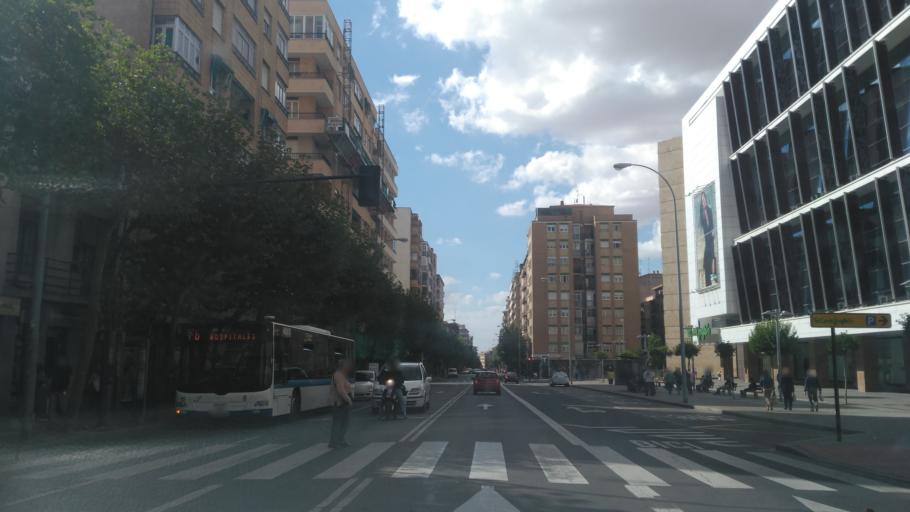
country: ES
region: Castille and Leon
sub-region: Provincia de Salamanca
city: Salamanca
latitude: 40.9741
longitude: -5.6565
